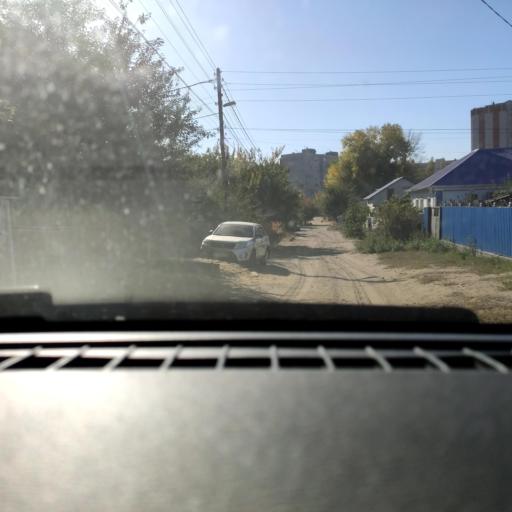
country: RU
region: Voronezj
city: Voronezh
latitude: 51.6648
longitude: 39.2861
